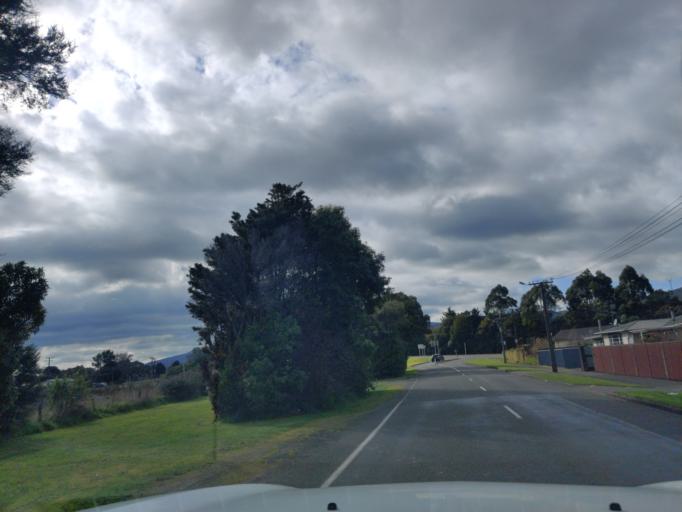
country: NZ
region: Manawatu-Wanganui
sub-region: Palmerston North City
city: Palmerston North
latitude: -40.2972
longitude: 175.7514
